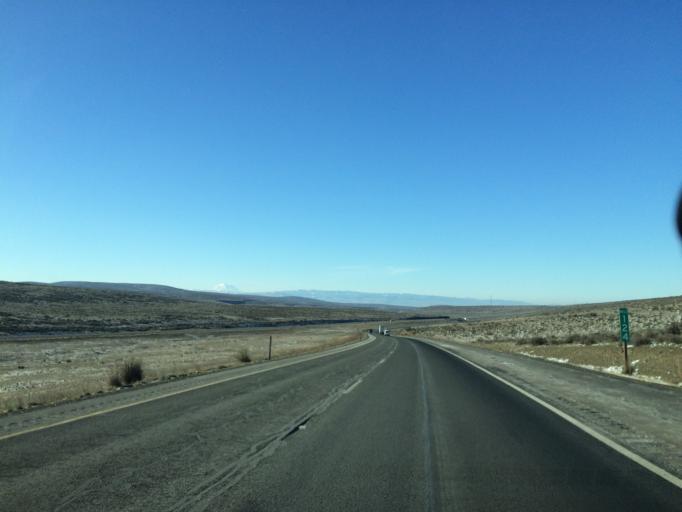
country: US
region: Washington
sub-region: Kittitas County
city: Kittitas
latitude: 46.9466
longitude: -120.2416
